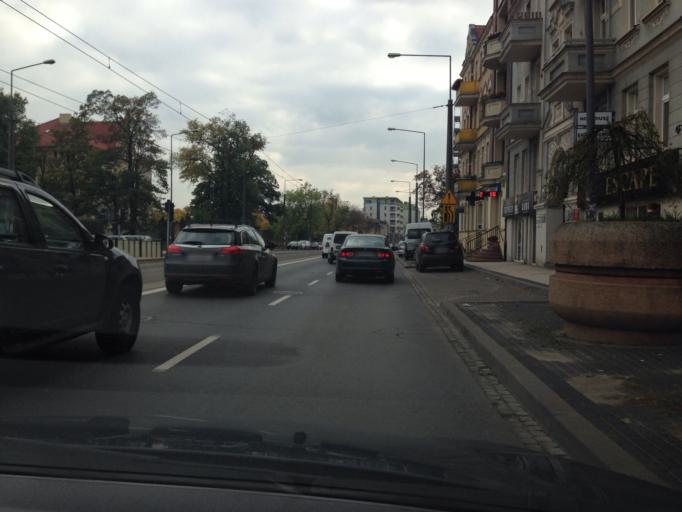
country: PL
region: Greater Poland Voivodeship
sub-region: Powiat poznanski
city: Lubon
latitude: 52.3872
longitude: 16.8910
